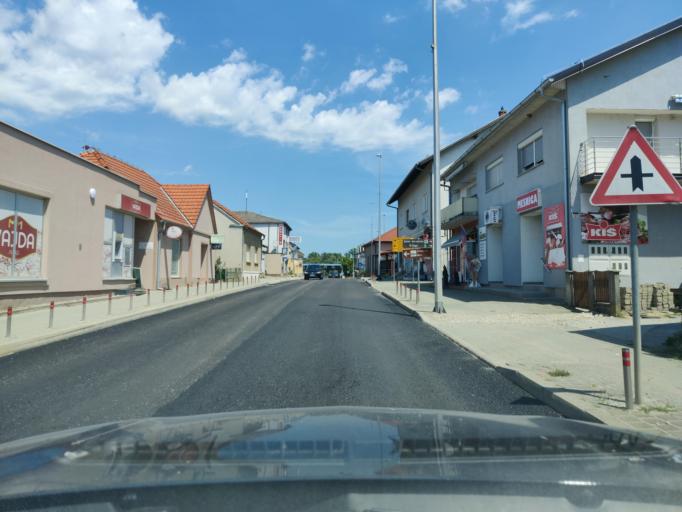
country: HR
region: Medimurska
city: Vratisinec
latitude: 46.5124
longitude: 16.4385
